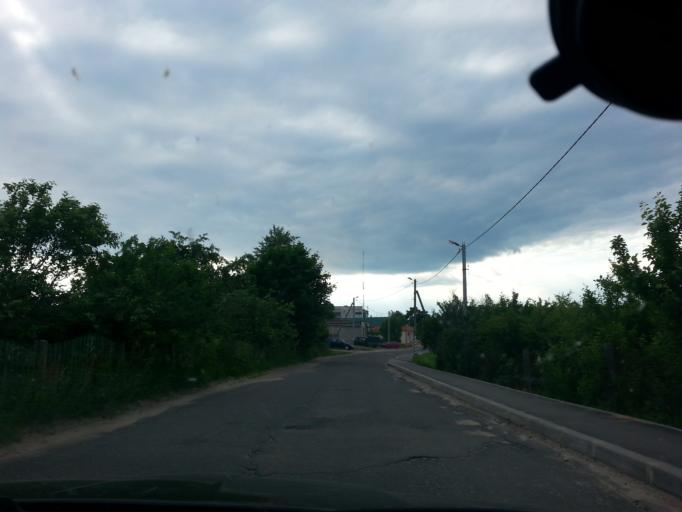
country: BY
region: Minsk
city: Myadzyel
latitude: 54.8665
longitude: 26.9373
